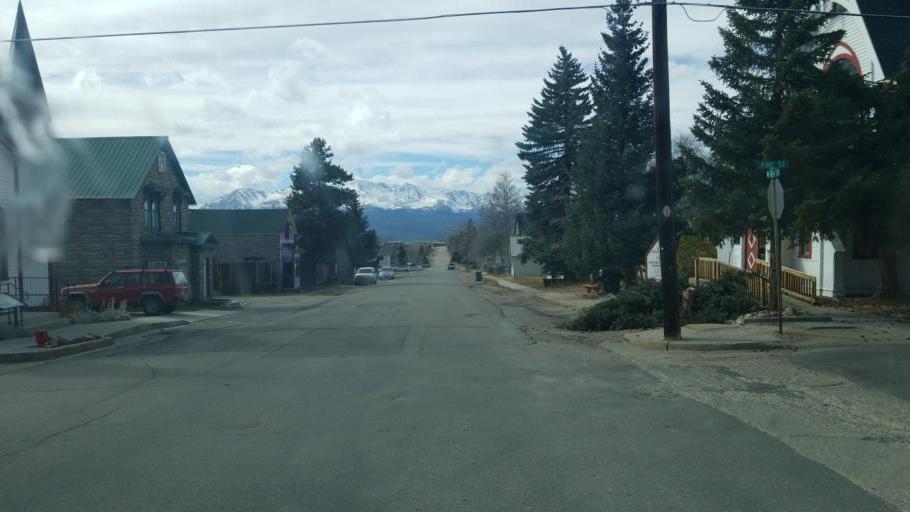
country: US
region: Colorado
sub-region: Lake County
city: Leadville
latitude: 39.2466
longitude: -106.2934
